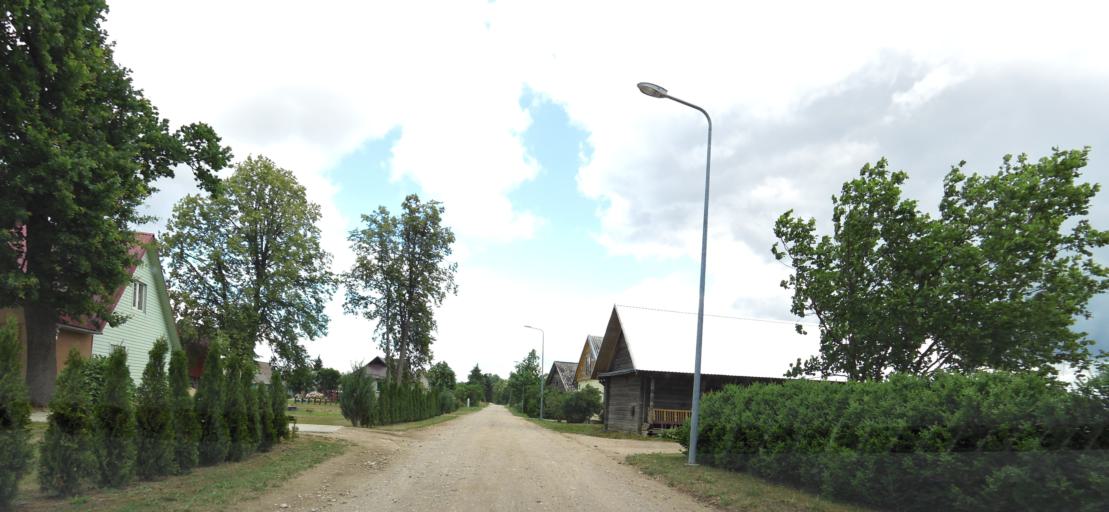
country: LT
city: Kupiskis
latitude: 55.8392
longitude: 24.9348
